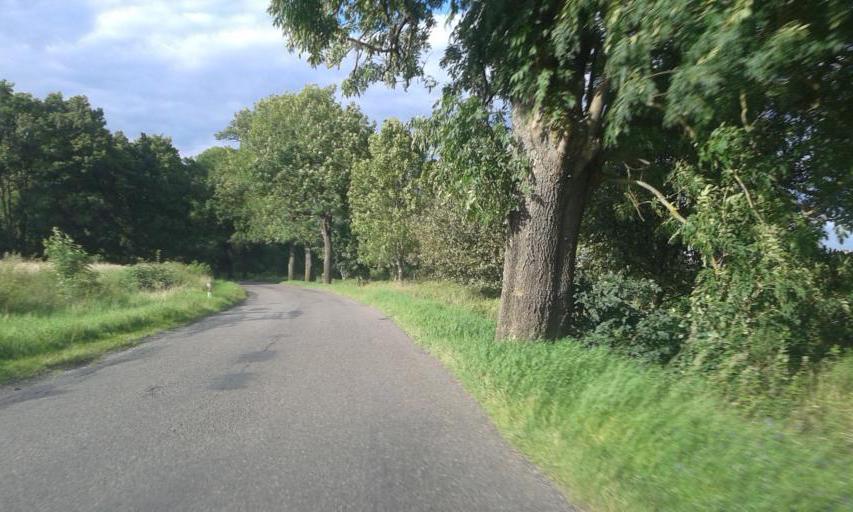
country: PL
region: West Pomeranian Voivodeship
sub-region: Powiat bialogardzki
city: Tychowo
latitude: 53.9072
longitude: 16.2420
